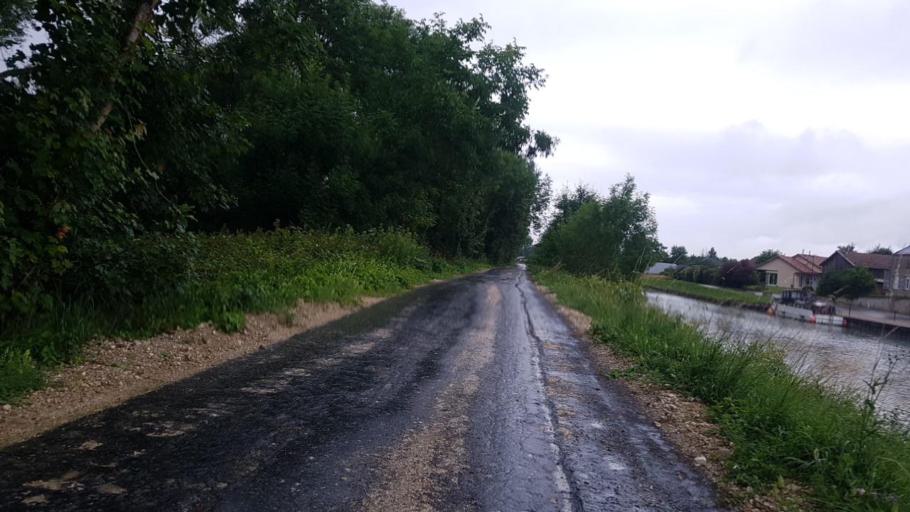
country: FR
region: Champagne-Ardenne
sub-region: Departement de la Marne
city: Sarry
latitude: 48.8572
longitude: 4.4801
